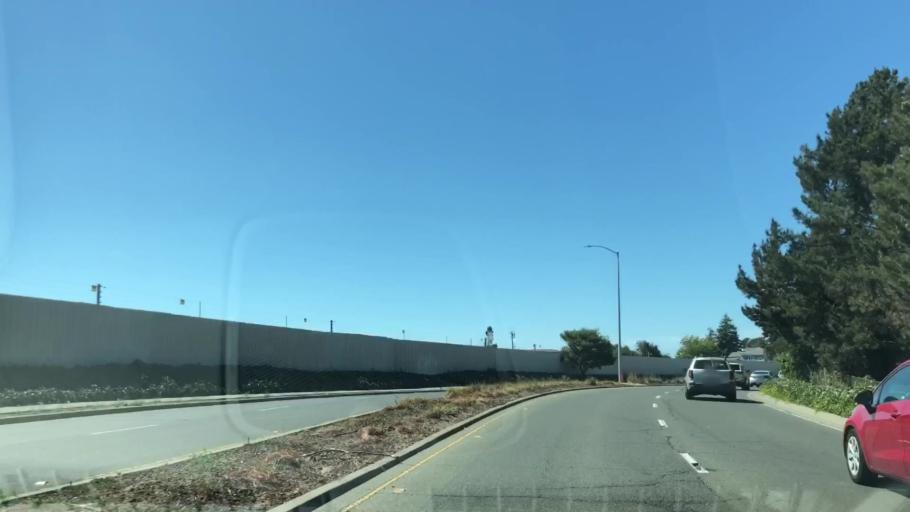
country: US
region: California
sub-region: Solano County
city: Vallejo
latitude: 38.0951
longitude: -122.2432
